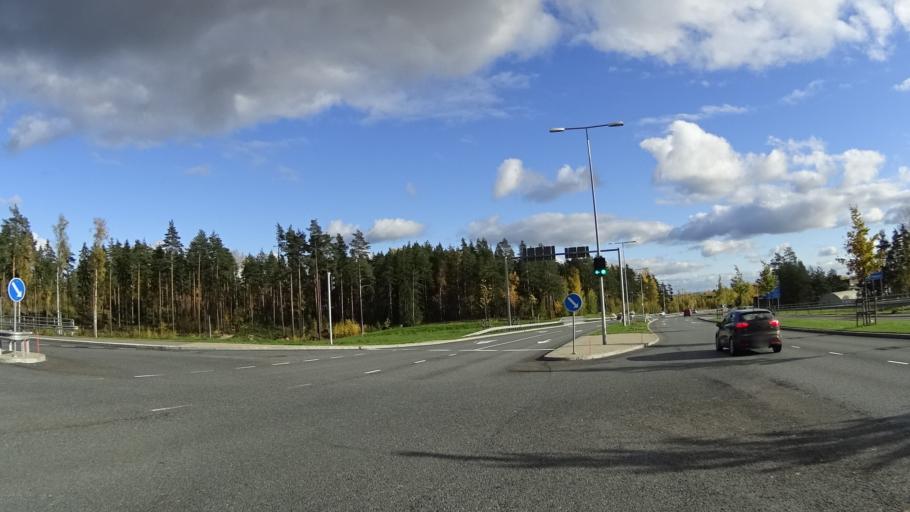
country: FI
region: Uusimaa
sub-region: Helsinki
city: Vantaa
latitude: 60.3013
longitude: 24.9631
